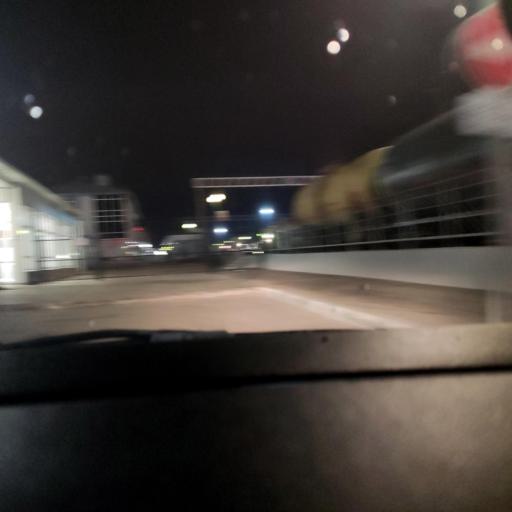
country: RU
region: Voronezj
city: Voronezh
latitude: 51.6392
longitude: 39.2580
